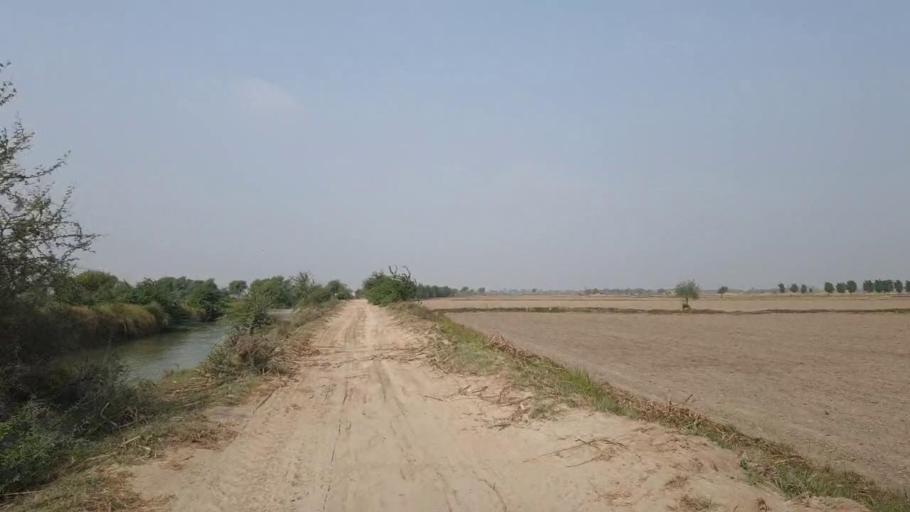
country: PK
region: Sindh
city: Kario
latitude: 24.8507
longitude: 68.5303
